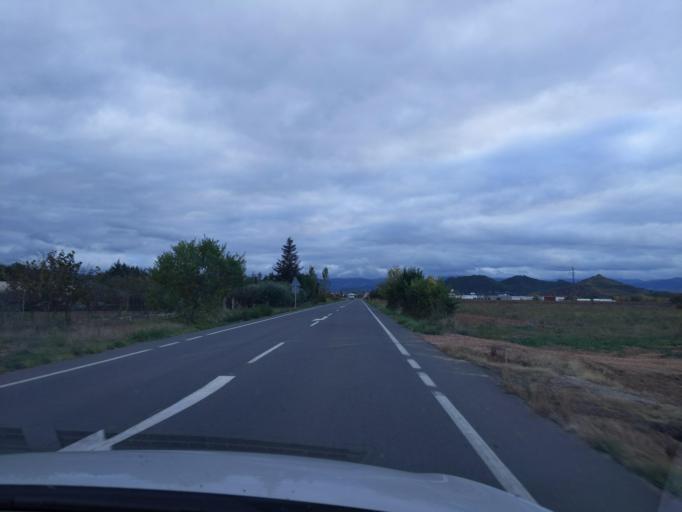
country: ES
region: La Rioja
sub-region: Provincia de La Rioja
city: Urunuela
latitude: 42.4329
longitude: -2.7152
